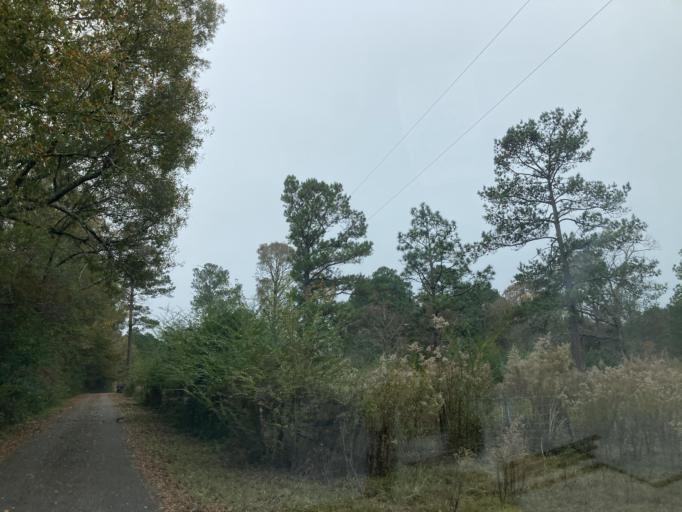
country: US
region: Mississippi
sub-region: Lamar County
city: Lumberton
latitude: 31.0236
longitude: -89.3595
